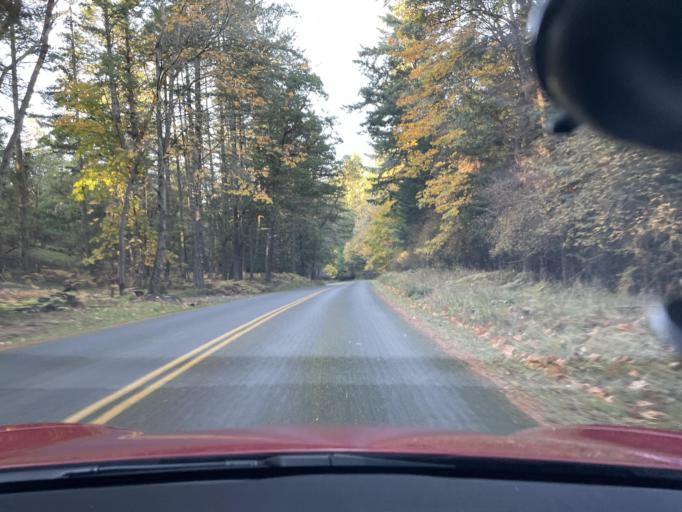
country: US
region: Washington
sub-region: San Juan County
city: Friday Harbor
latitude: 48.5352
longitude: -123.1591
